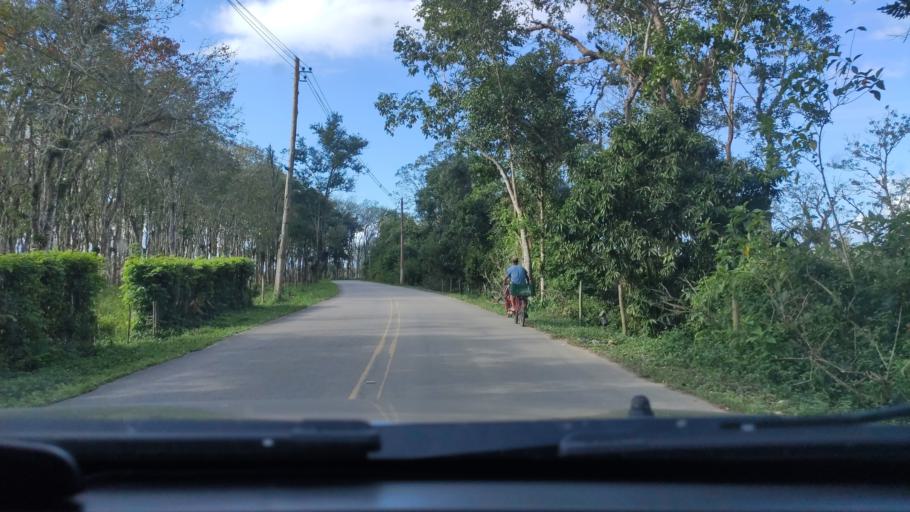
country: BR
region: Sao Paulo
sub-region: Sao Sebastiao
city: Sao Sebastiao
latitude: -23.6974
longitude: -45.4667
